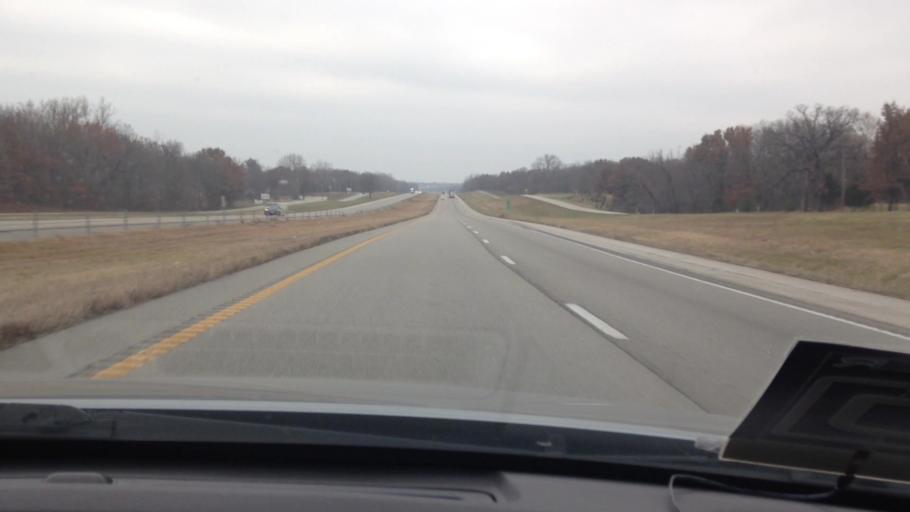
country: US
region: Missouri
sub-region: Cass County
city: Peculiar
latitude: 38.6795
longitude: -94.4204
